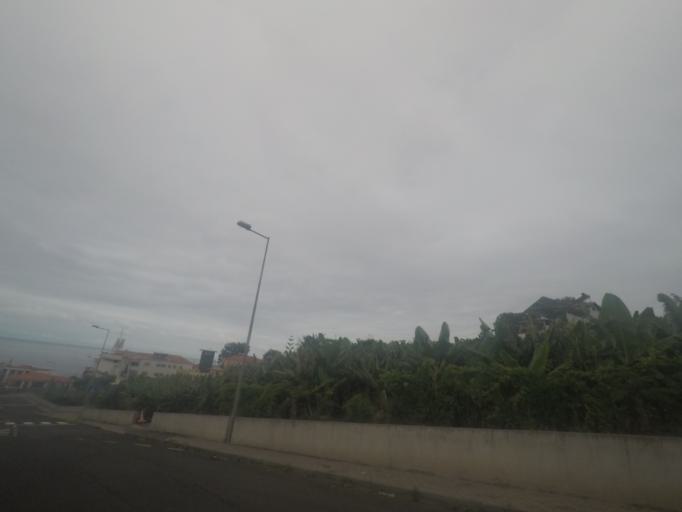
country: PT
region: Madeira
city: Camara de Lobos
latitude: 32.6556
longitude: -16.9833
